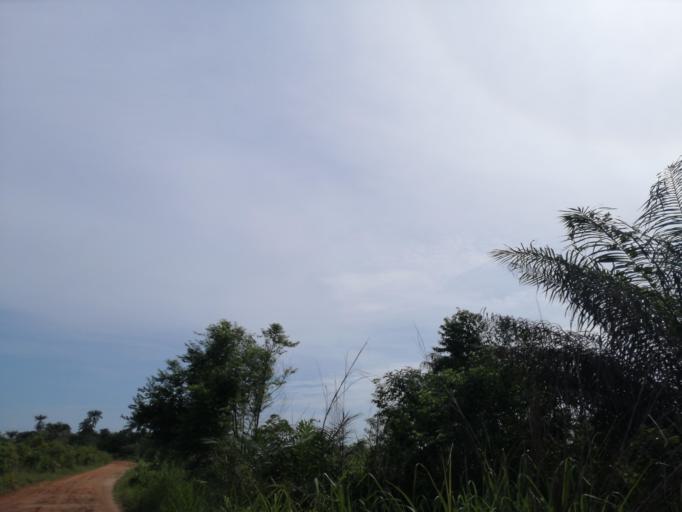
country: SL
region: Northern Province
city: Port Loko
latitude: 8.7937
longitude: -12.9237
